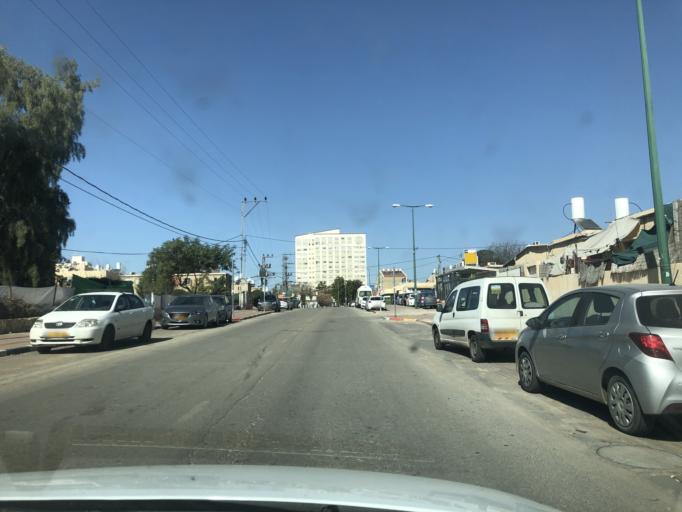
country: IL
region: Southern District
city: Beersheba
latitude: 31.2603
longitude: 34.7950
